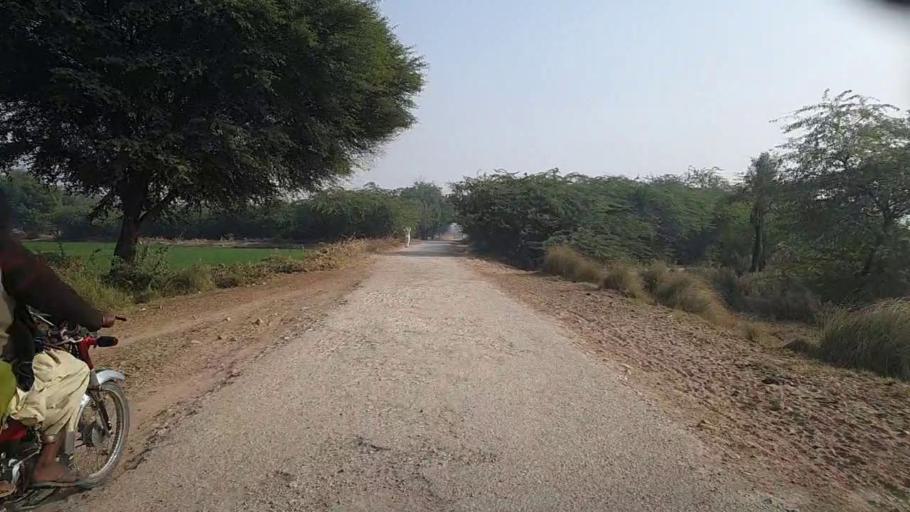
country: PK
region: Sindh
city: Setharja Old
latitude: 27.0599
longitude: 68.4600
